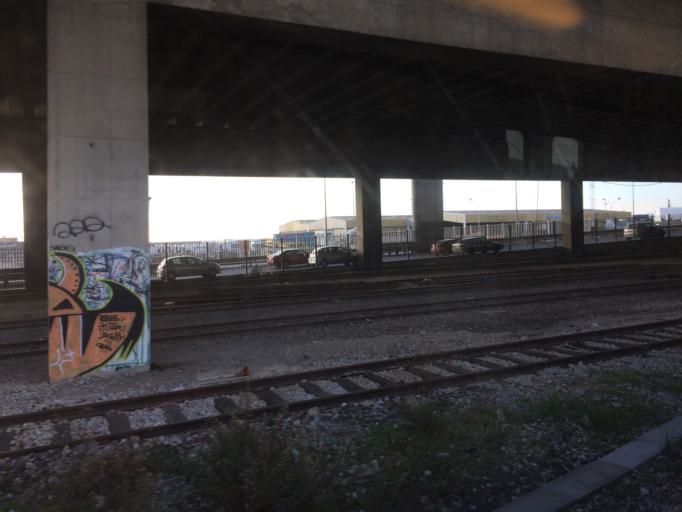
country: FR
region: Provence-Alpes-Cote d'Azur
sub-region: Departement des Bouches-du-Rhone
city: Marseille 03
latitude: 43.3162
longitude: 5.3652
